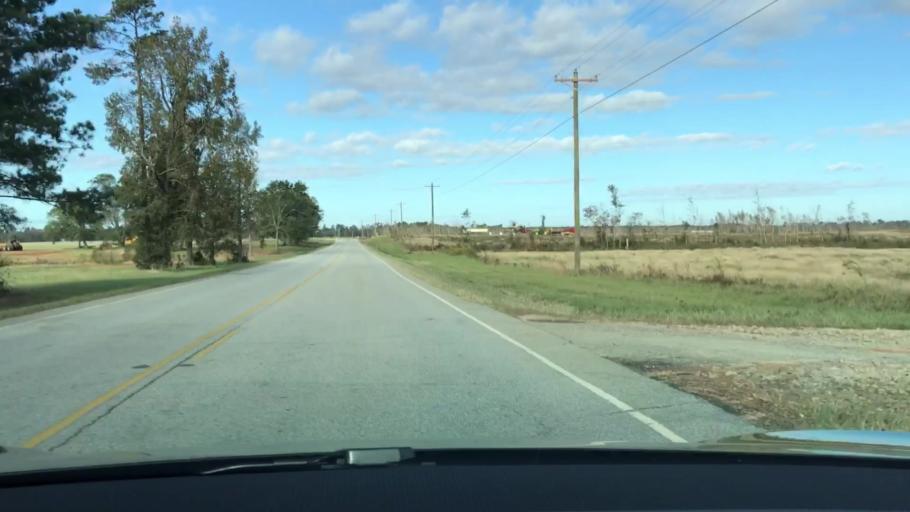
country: US
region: Georgia
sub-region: Jefferson County
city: Wrens
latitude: 33.1145
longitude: -82.4338
